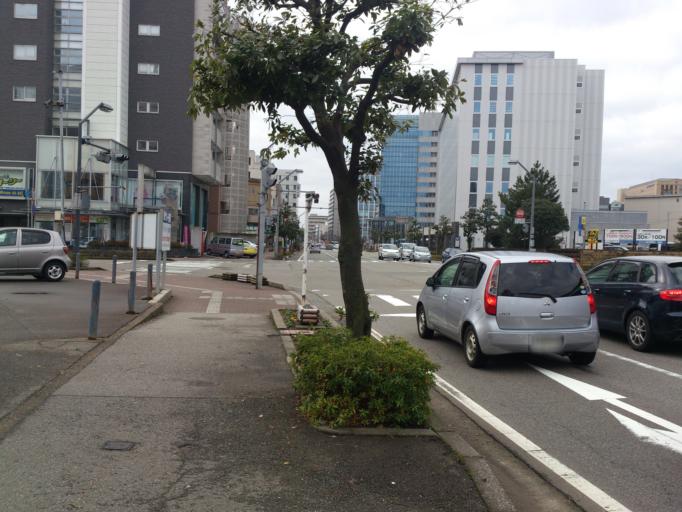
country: JP
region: Ishikawa
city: Kanazawa-shi
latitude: 36.5821
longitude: 136.6476
